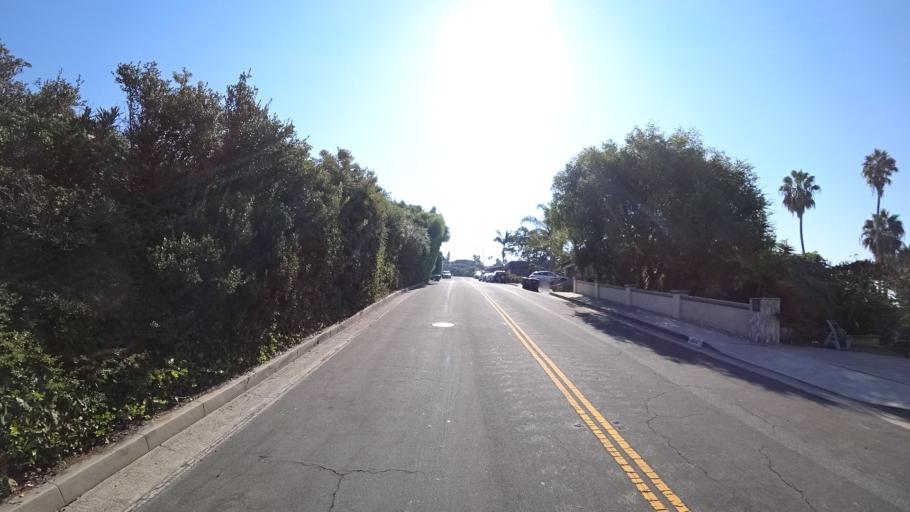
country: US
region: California
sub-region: Orange County
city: San Clemente
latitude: 33.4342
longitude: -117.6133
